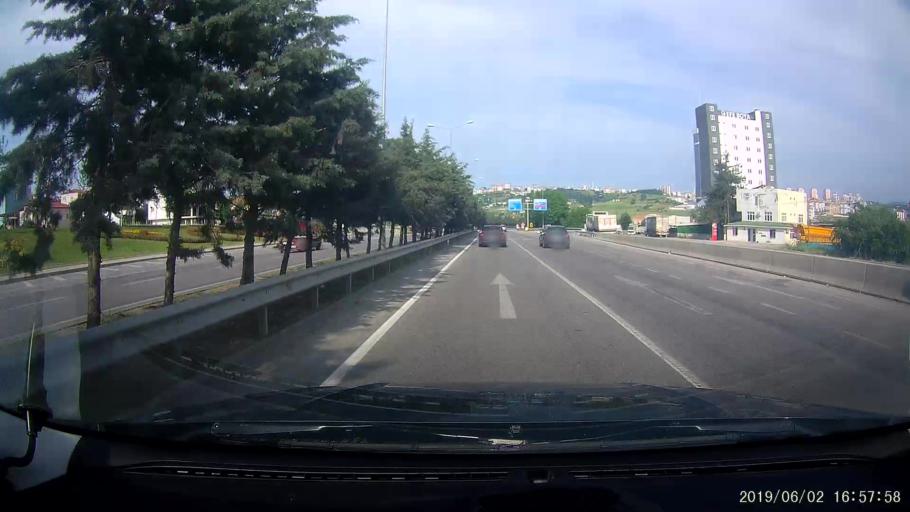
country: TR
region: Samsun
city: Samsun
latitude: 41.2902
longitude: 36.2824
